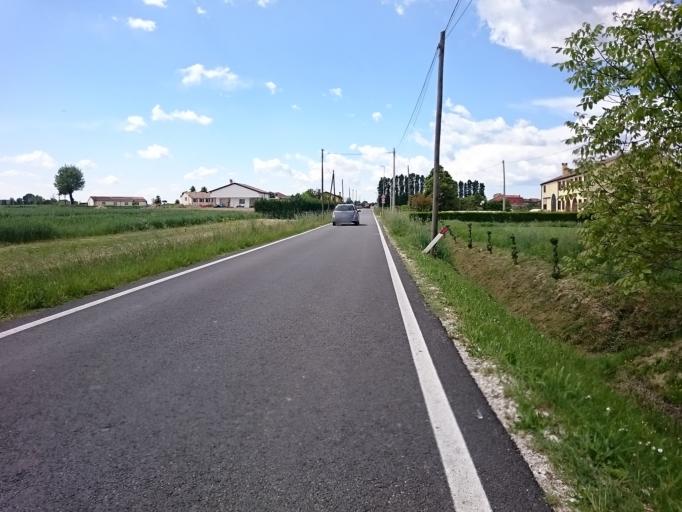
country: IT
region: Veneto
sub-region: Provincia di Padova
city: Casalserugo
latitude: 45.3322
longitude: 11.9313
